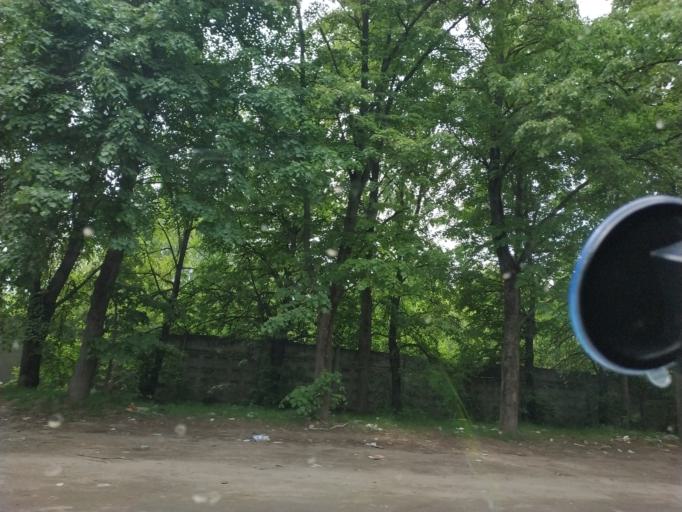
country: RU
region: Moskovskaya
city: Zhukovskiy
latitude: 55.5579
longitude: 38.1129
